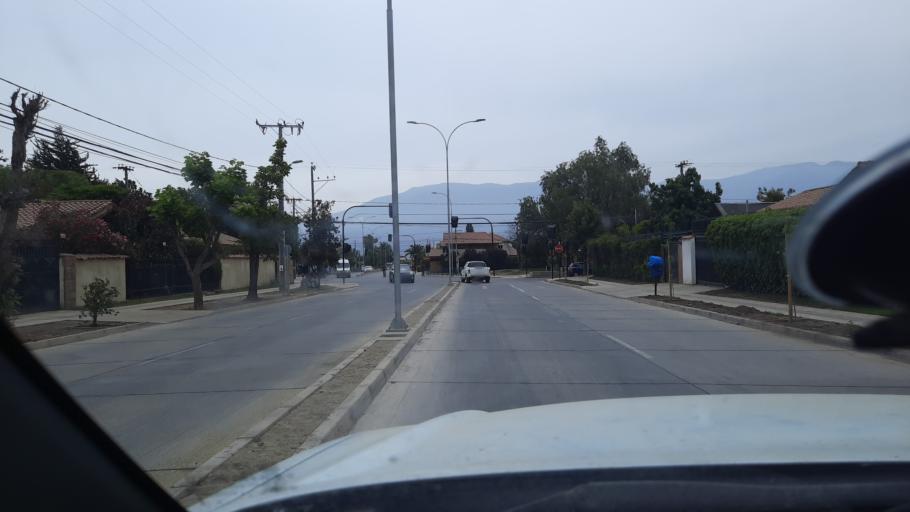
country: CL
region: Valparaiso
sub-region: Provincia de San Felipe
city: San Felipe
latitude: -32.7438
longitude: -70.7163
